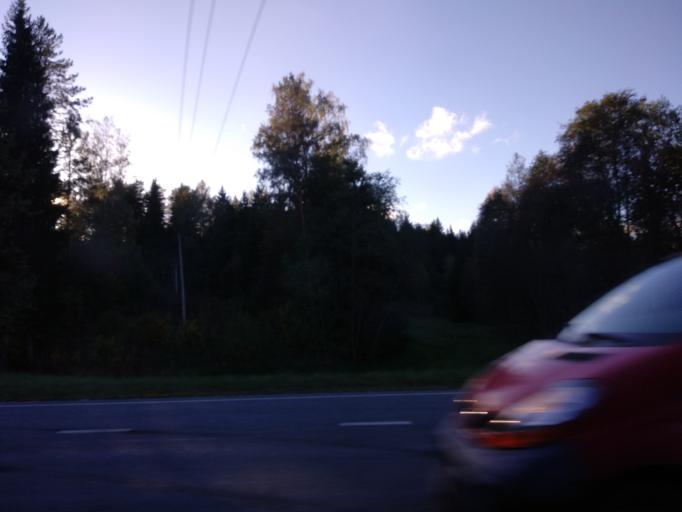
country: EE
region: Polvamaa
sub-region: Polva linn
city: Polva
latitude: 58.0429
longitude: 27.0658
